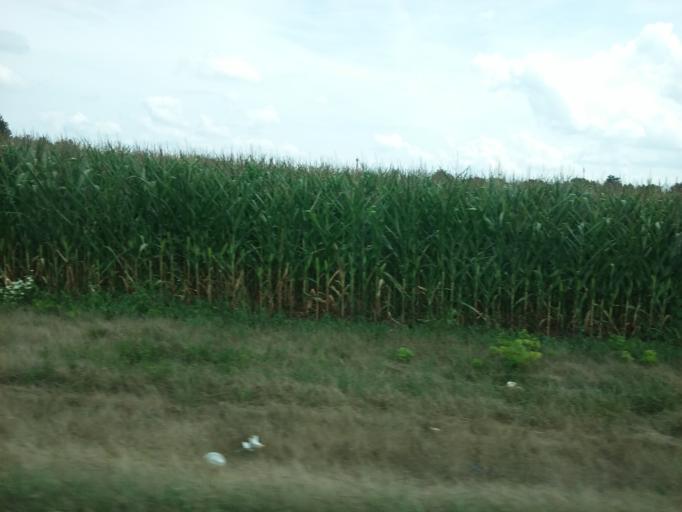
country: US
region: Ohio
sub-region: Hancock County
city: Findlay
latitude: 41.0432
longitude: -83.6887
